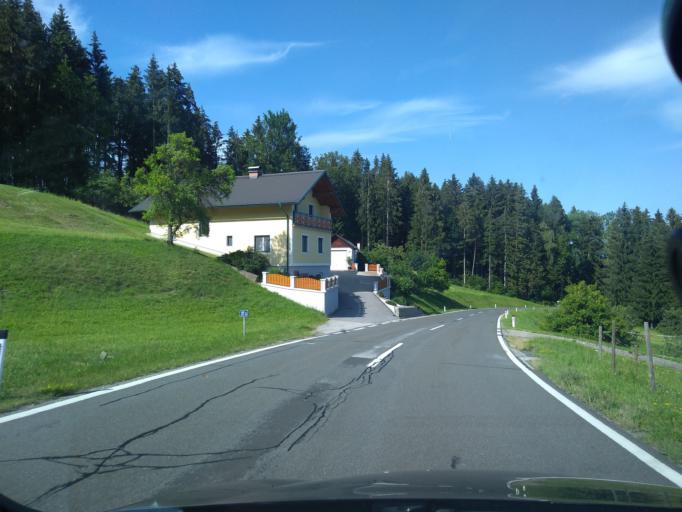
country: AT
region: Styria
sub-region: Politischer Bezirk Graz-Umgebung
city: Semriach
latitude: 47.2677
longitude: 15.4277
